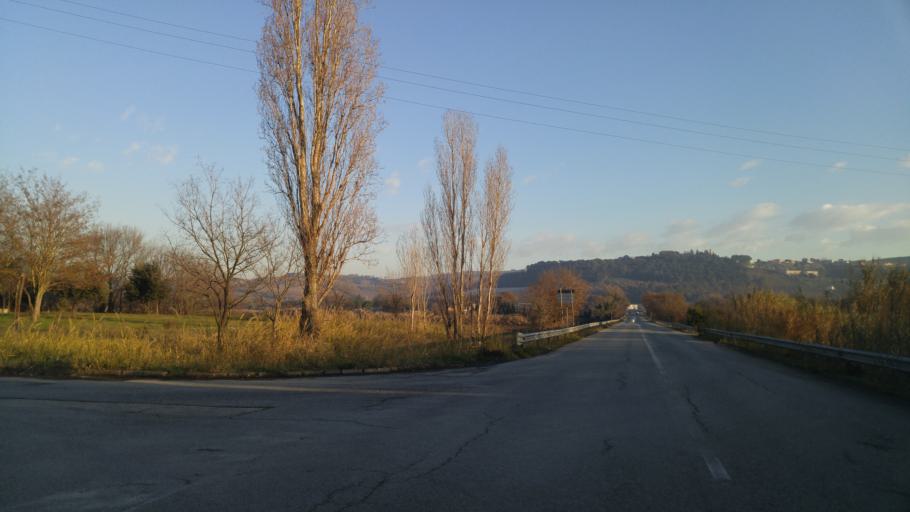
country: IT
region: The Marches
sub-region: Provincia di Ancona
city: Monterado
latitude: 43.7085
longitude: 13.0775
